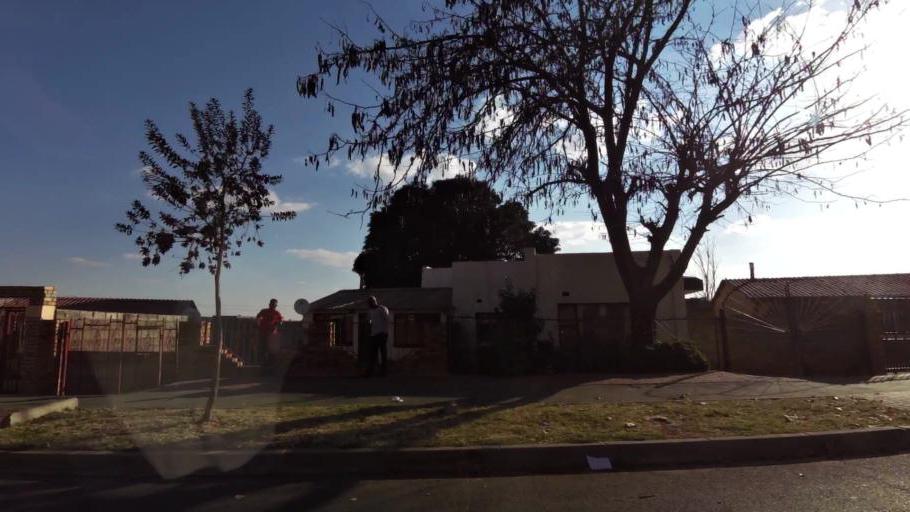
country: ZA
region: Gauteng
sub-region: City of Johannesburg Metropolitan Municipality
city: Roodepoort
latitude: -26.2088
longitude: 27.8844
